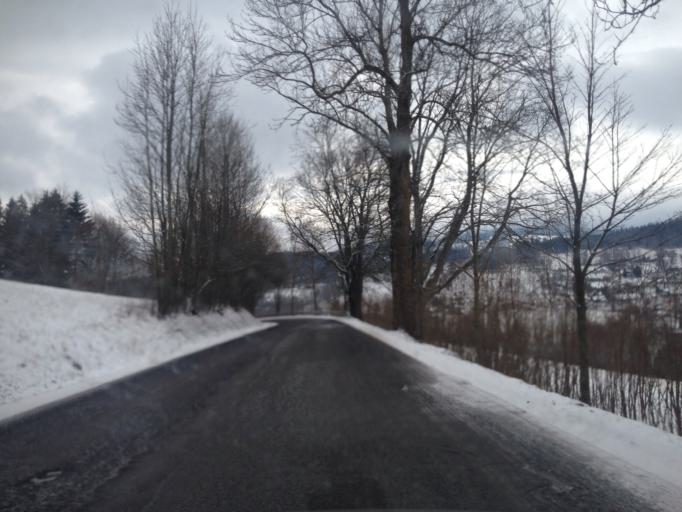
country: CZ
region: Liberecky
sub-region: Okres Semily
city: Vysoke nad Jizerou
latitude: 50.6974
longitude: 15.3888
